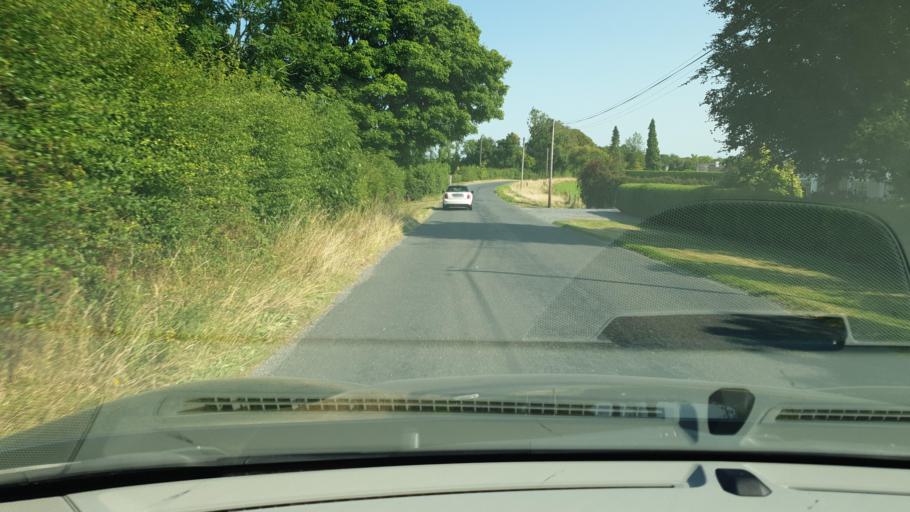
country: IE
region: Leinster
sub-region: An Mhi
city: Athboy
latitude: 53.6286
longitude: -6.9534
